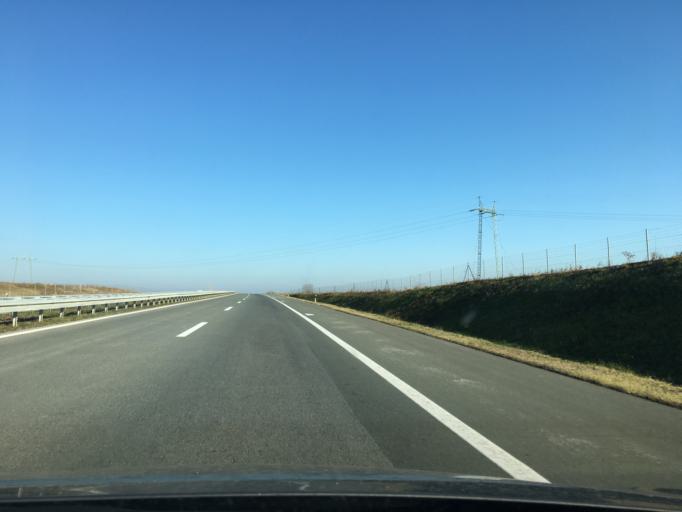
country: RS
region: Autonomna Pokrajina Vojvodina
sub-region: Severnobacki Okrug
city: Mali Igos
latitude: 45.6530
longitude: 19.7222
